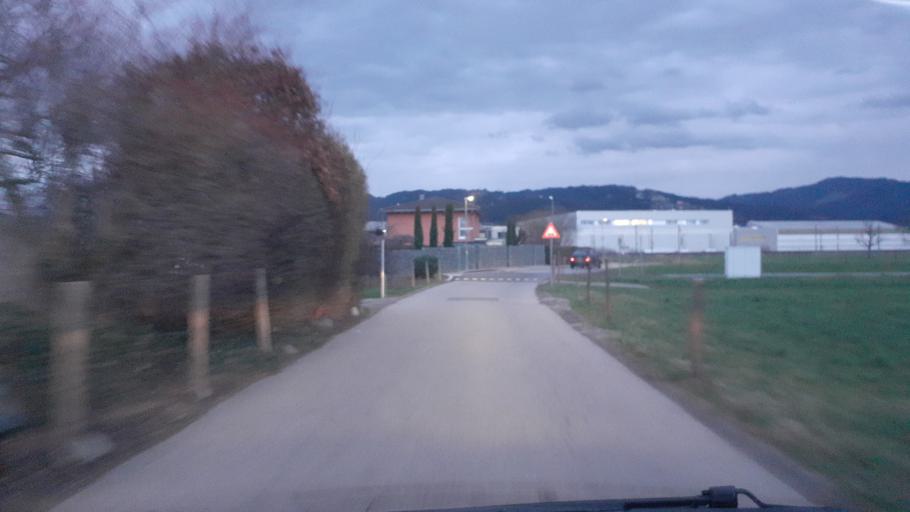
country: AT
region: Vorarlberg
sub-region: Politischer Bezirk Bregenz
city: Lauterach
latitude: 47.4705
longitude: 9.7228
